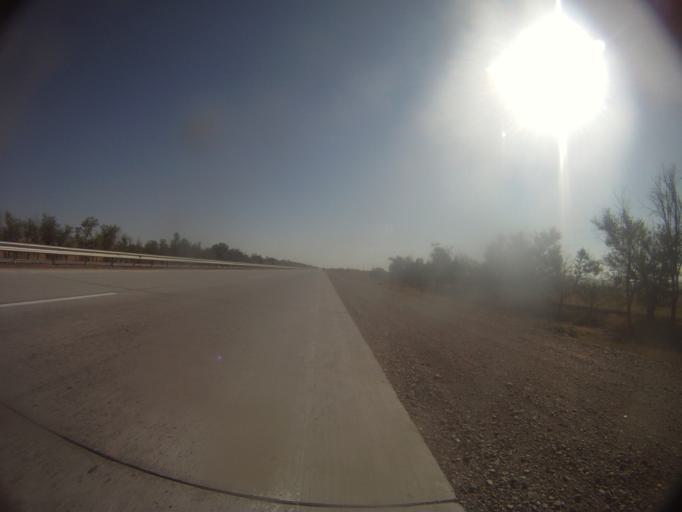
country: KZ
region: Ongtustik Qazaqstan
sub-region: Tulkibas Audany
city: Zhabagly
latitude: 42.7056
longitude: 70.8402
